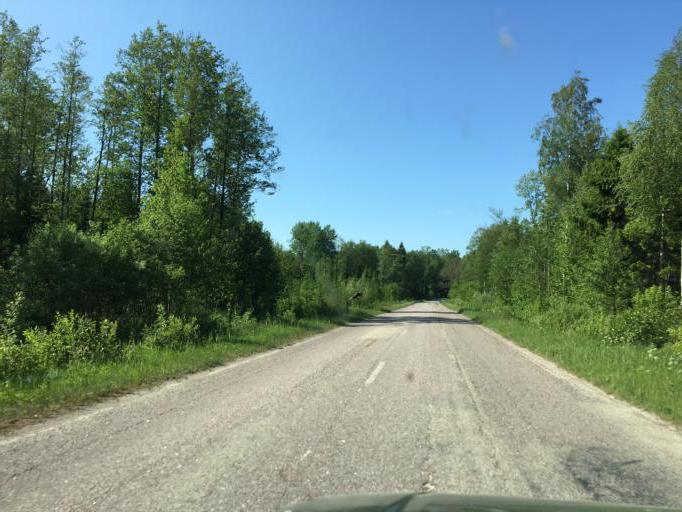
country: LV
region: Ventspils
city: Ventspils
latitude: 57.4948
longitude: 21.8110
